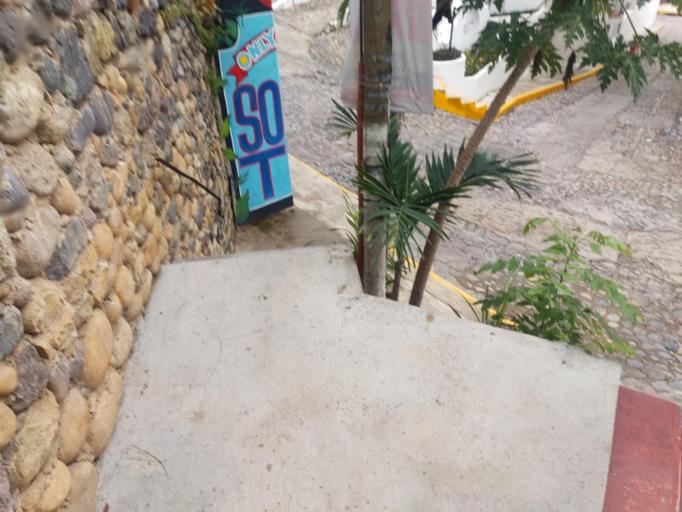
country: MX
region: Jalisco
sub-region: Puerto Vallarta
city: Puerto Vallarta
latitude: 20.5979
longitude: -105.2384
